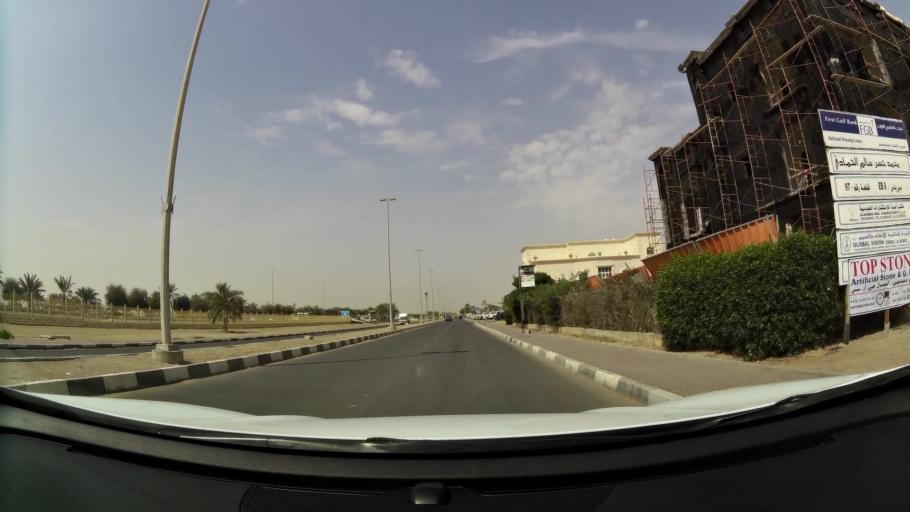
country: AE
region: Abu Dhabi
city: Abu Dhabi
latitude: 24.2923
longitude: 54.6344
